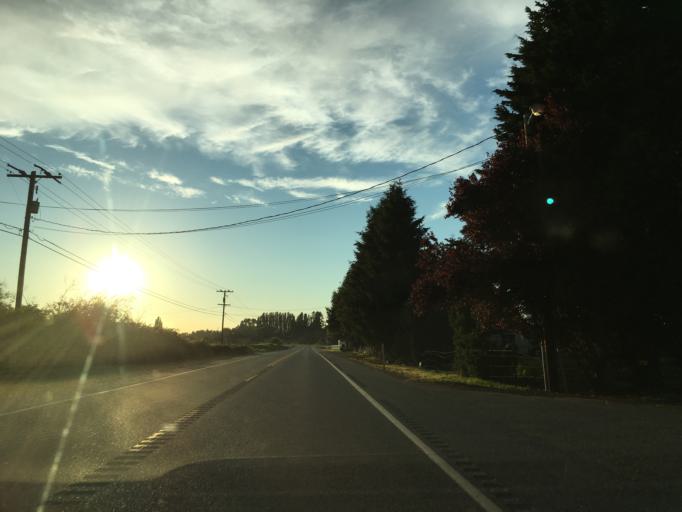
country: US
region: Washington
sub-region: Skagit County
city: Burlington
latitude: 48.5118
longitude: -122.3726
